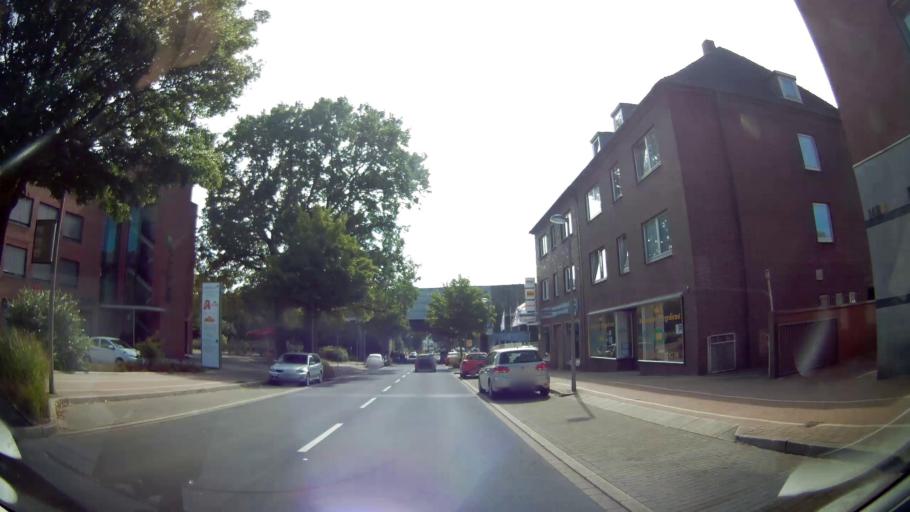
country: DE
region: North Rhine-Westphalia
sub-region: Regierungsbezirk Munster
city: Gladbeck
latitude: 51.5591
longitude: 7.0006
